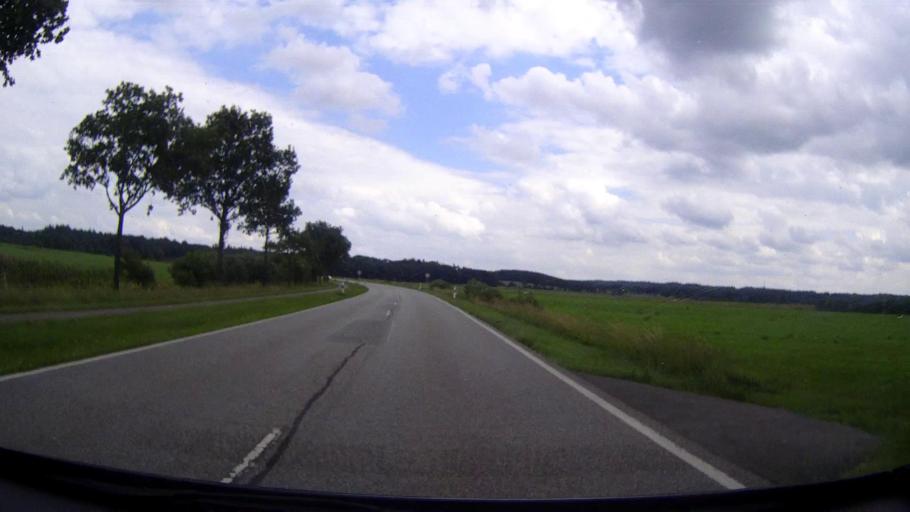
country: DE
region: Schleswig-Holstein
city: Tappendorf
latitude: 54.0808
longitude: 9.6974
